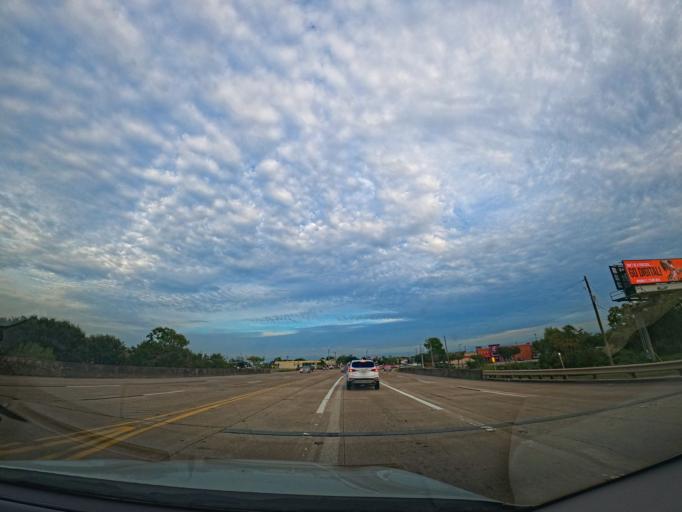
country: US
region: Texas
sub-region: Galveston County
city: League City
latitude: 29.5226
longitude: -95.0792
